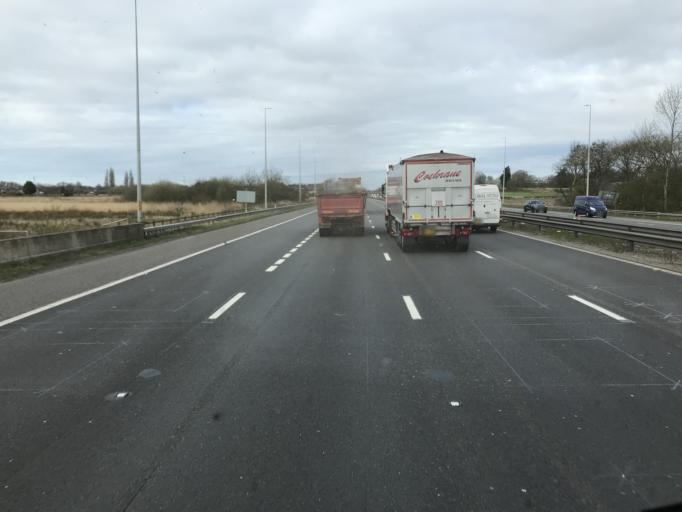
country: GB
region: England
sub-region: Warrington
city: Winwick
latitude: 53.4230
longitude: -2.5859
